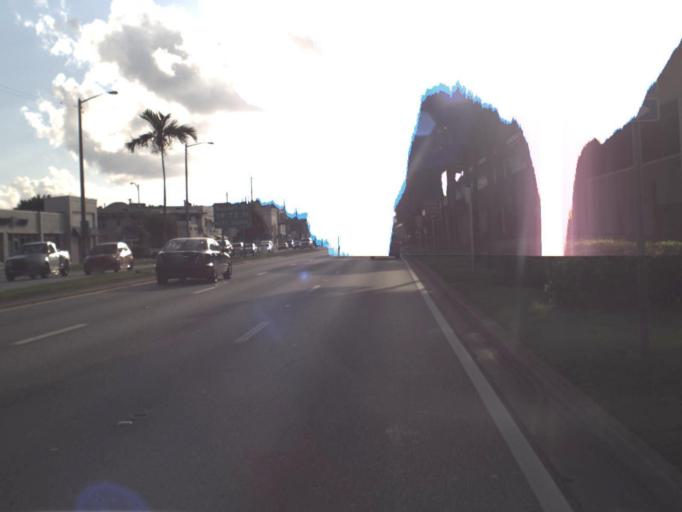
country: US
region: Florida
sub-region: Miami-Dade County
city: South Miami
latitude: 25.7057
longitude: -80.2881
